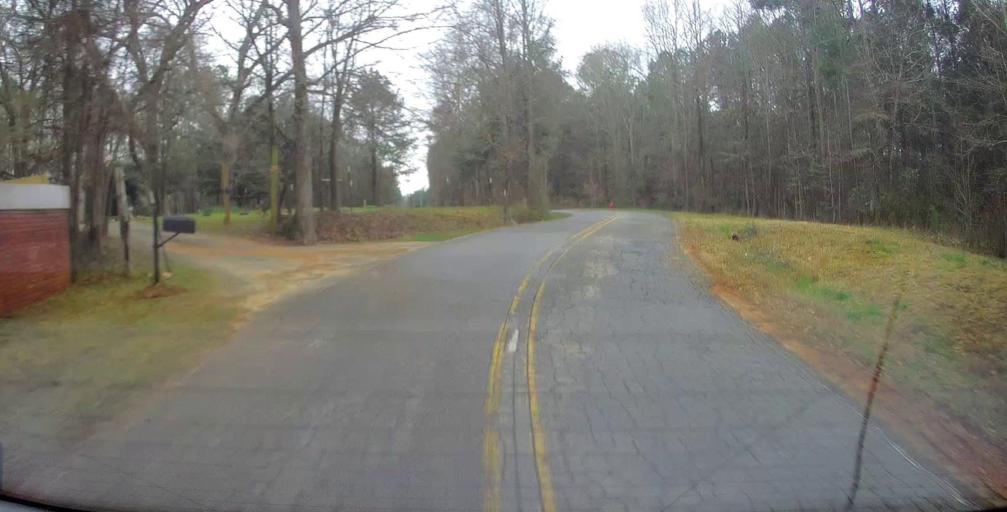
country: US
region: Georgia
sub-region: Monroe County
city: Forsyth
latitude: 33.0117
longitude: -83.8223
